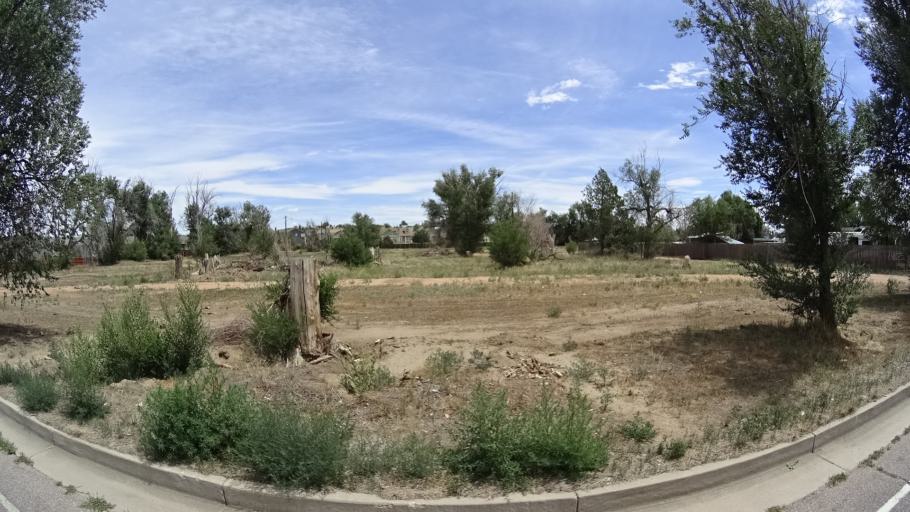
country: US
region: Colorado
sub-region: El Paso County
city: Fountain
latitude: 38.6784
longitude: -104.6874
